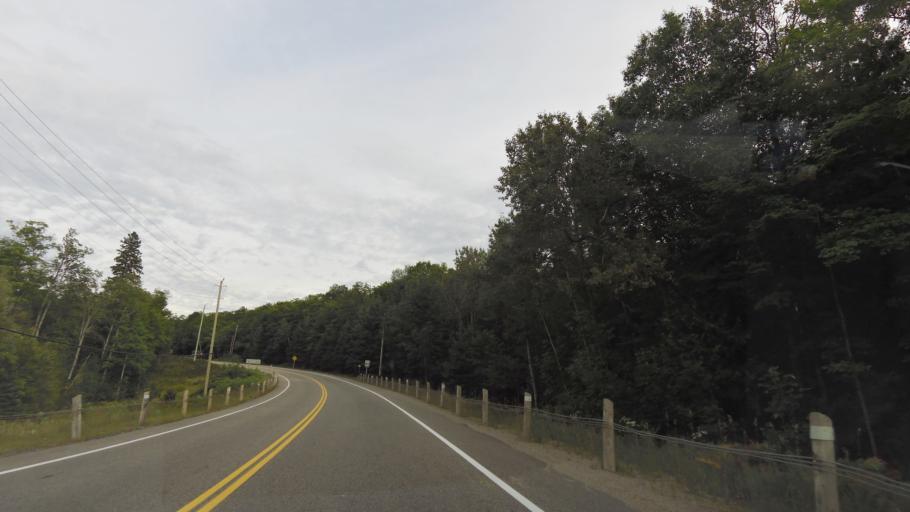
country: CA
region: Ontario
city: Bancroft
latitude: 45.0407
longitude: -78.4843
